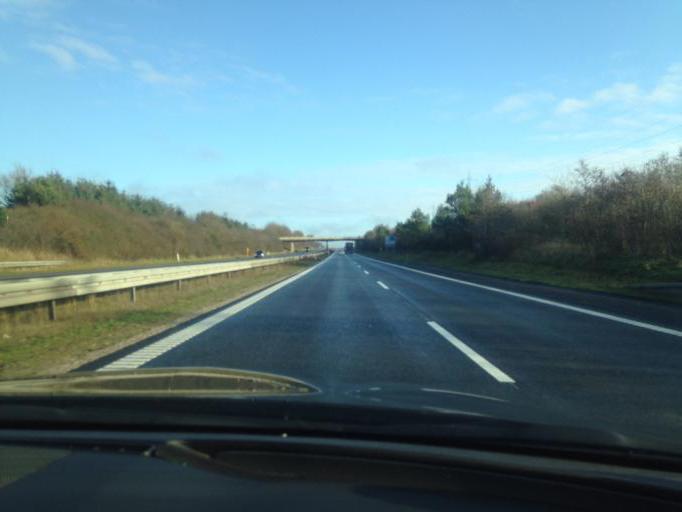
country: DK
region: South Denmark
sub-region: Kolding Kommune
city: Lunderskov
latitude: 55.5095
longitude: 9.3662
